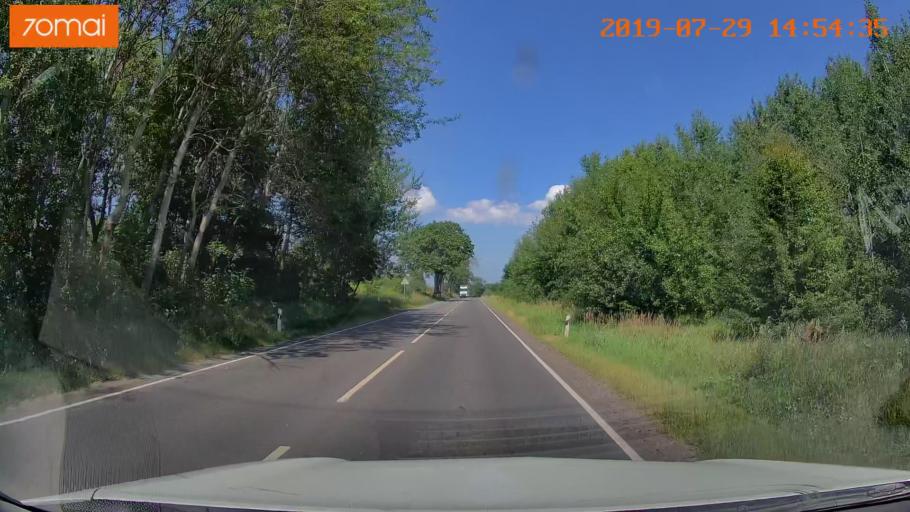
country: RU
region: Kaliningrad
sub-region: Gorod Kaliningrad
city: Baltiysk
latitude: 54.6752
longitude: 19.9256
